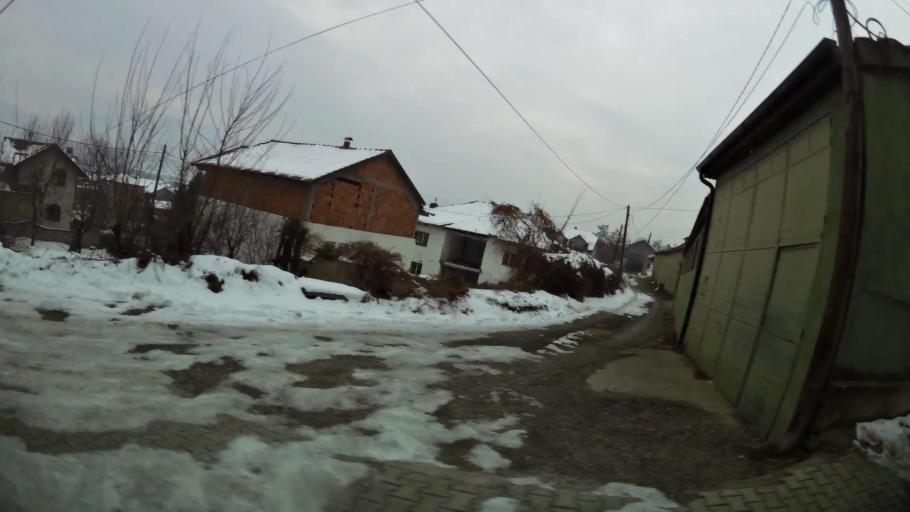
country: MK
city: Kondovo
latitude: 42.0123
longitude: 21.3162
